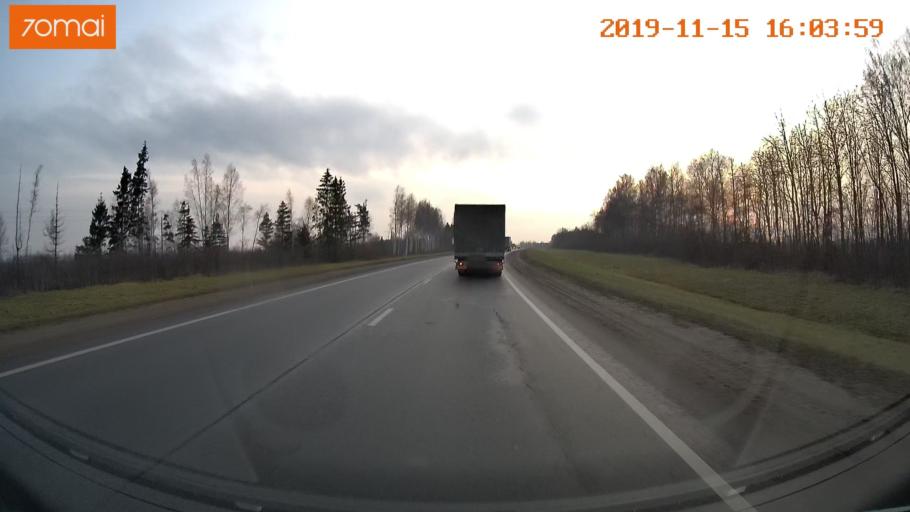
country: RU
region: Jaroslavl
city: Yaroslavl
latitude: 57.7526
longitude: 39.9076
